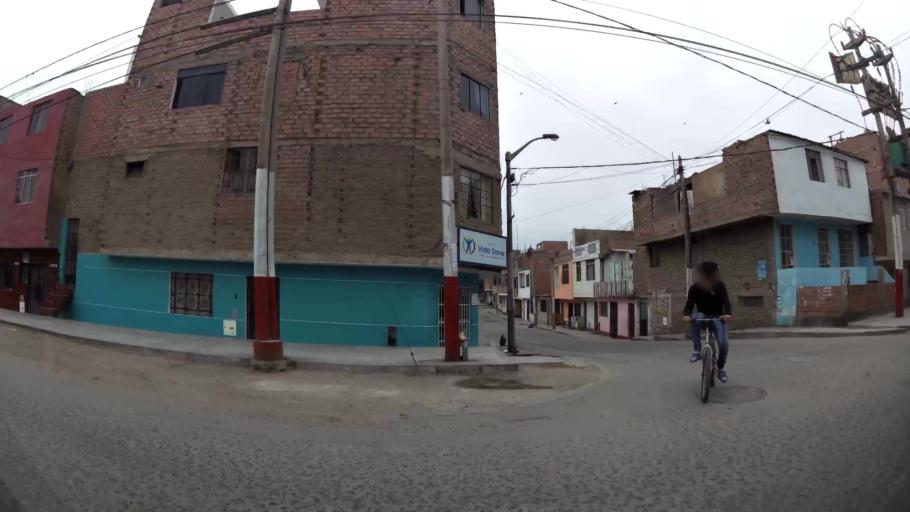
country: PE
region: Callao
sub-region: Callao
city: Callao
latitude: -12.0537
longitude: -77.1191
